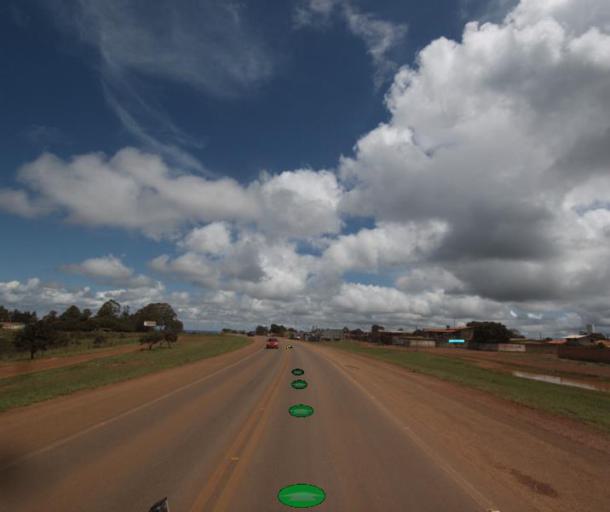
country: BR
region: Federal District
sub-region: Brasilia
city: Brasilia
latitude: -15.7374
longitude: -48.4070
